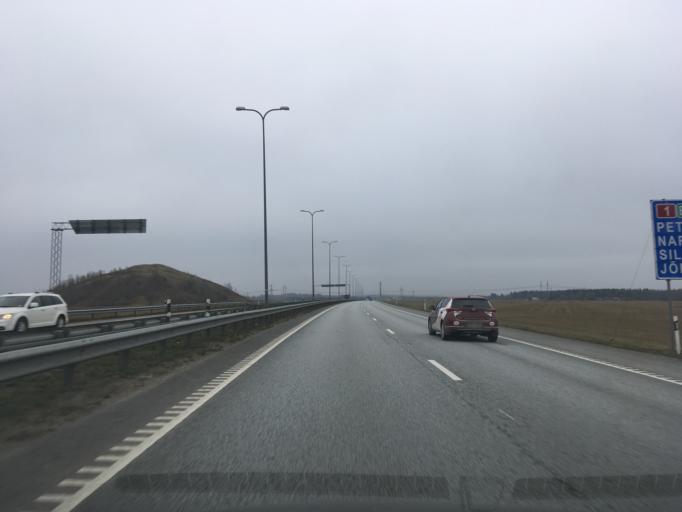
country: EE
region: Ida-Virumaa
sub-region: Kohtla-Jaerve linn
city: Kohtla-Jarve
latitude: 59.3982
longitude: 27.3331
